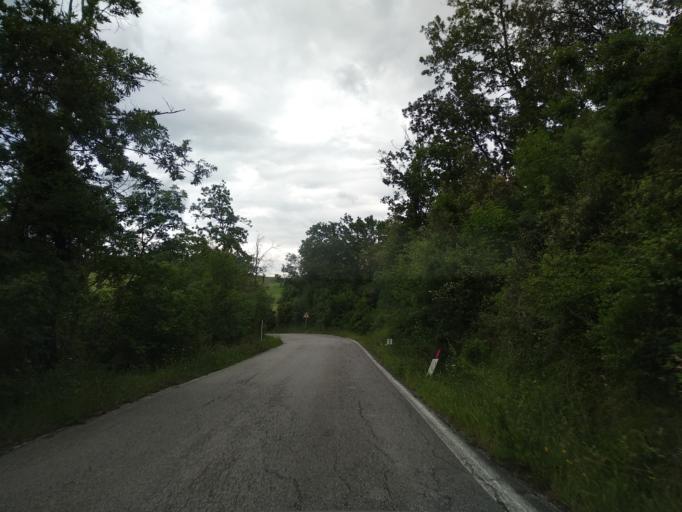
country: IT
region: Tuscany
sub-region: Provincia di Livorno
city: Guasticce
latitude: 43.5654
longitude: 10.4232
